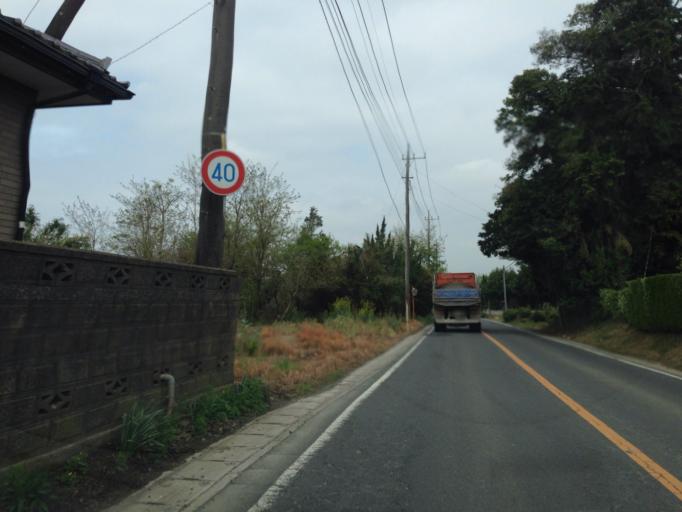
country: JP
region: Ibaraki
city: Ishige
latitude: 36.1685
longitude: 139.8845
